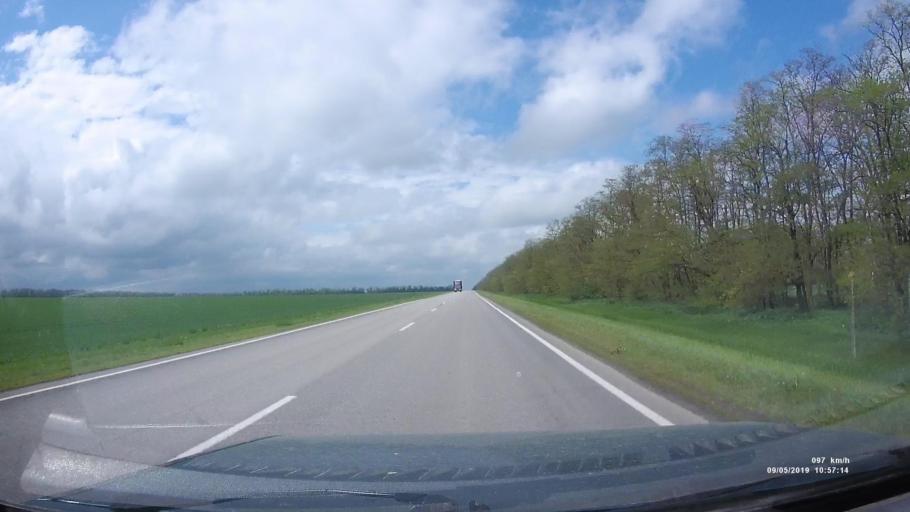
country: RU
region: Rostov
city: Peshkovo
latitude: 46.8662
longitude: 39.2835
